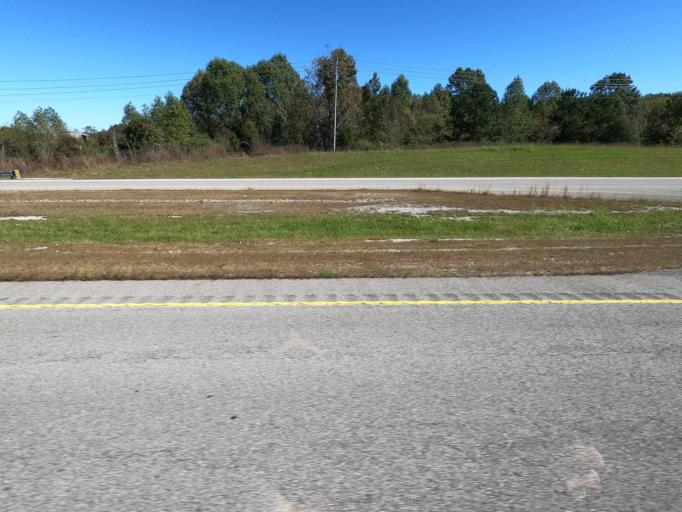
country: US
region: Tennessee
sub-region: Maury County
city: Mount Pleasant
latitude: 35.4573
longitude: -87.2687
